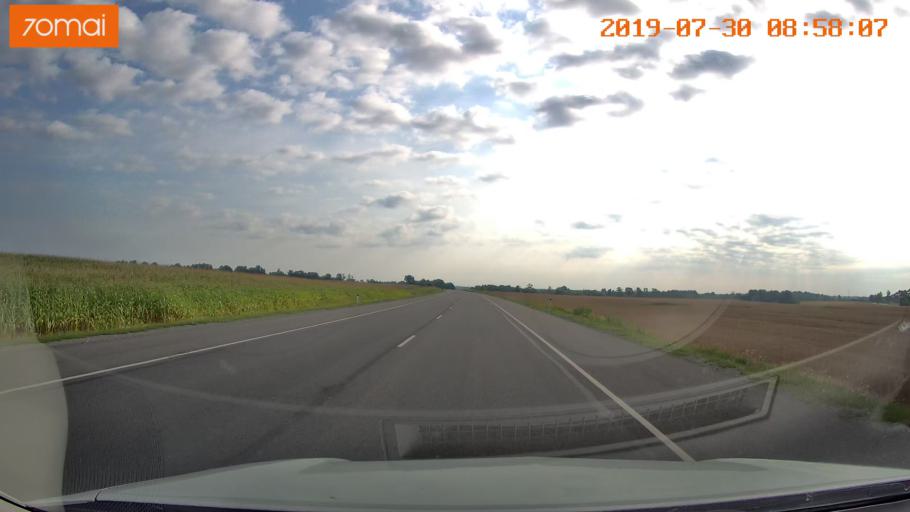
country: RU
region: Kaliningrad
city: Gusev
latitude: 54.6056
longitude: 22.1218
